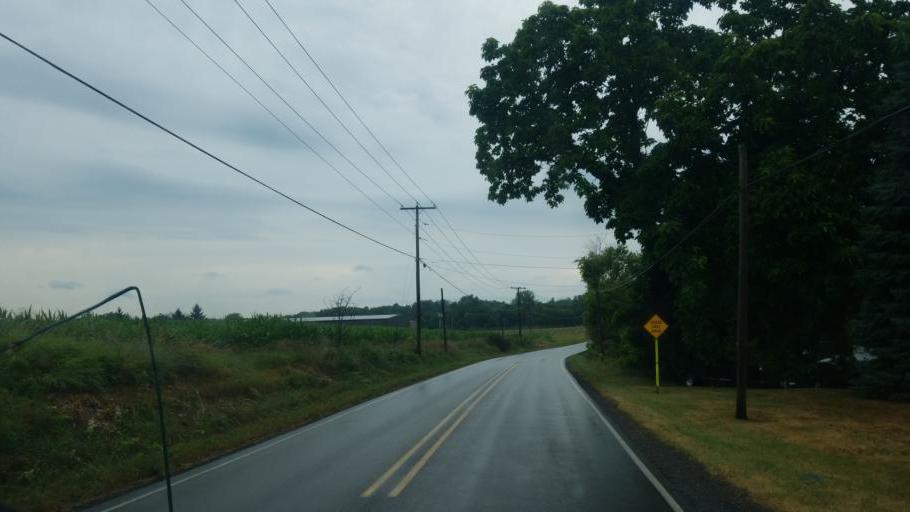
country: US
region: Indiana
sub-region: Steuben County
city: Hamilton
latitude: 41.5365
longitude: -84.9254
